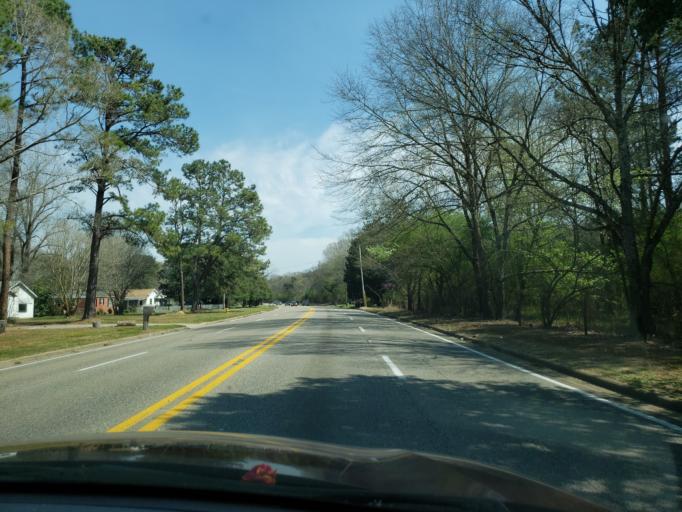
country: US
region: Alabama
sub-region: Elmore County
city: Wetumpka
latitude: 32.5345
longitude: -86.2368
